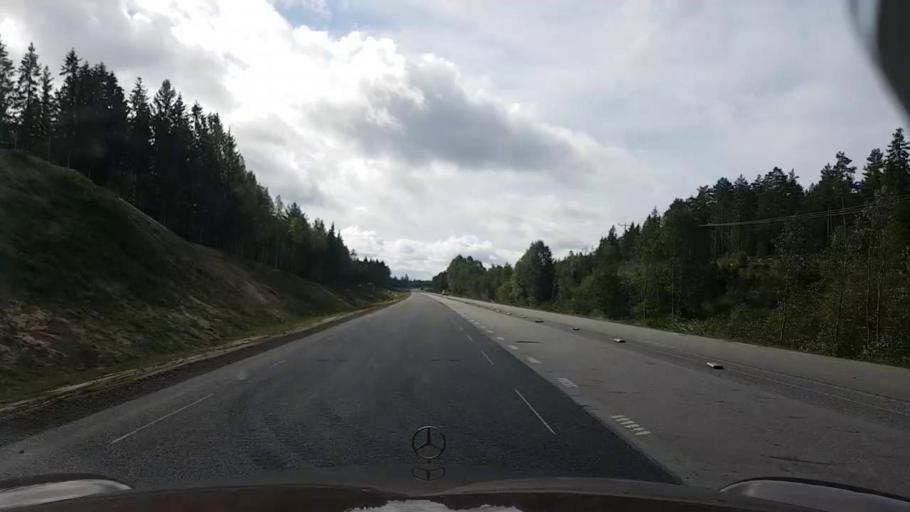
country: SE
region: OErebro
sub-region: Askersunds Kommun
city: Asbro
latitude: 58.9843
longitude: 15.0396
